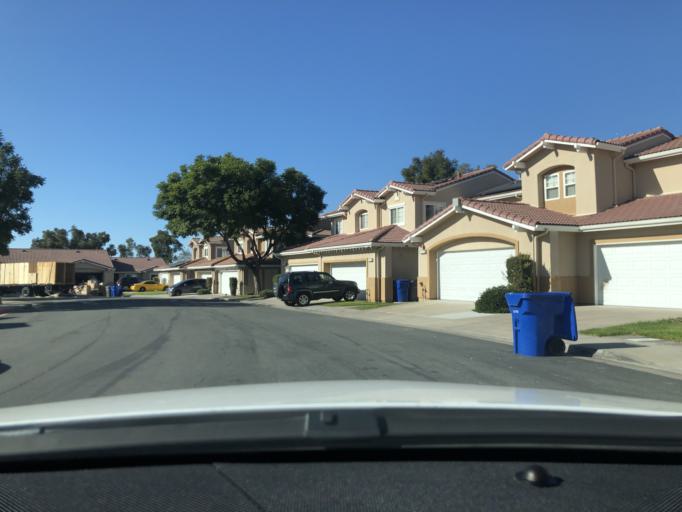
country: US
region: California
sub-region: San Diego County
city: Lemon Grove
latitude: 32.7411
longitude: -117.0655
